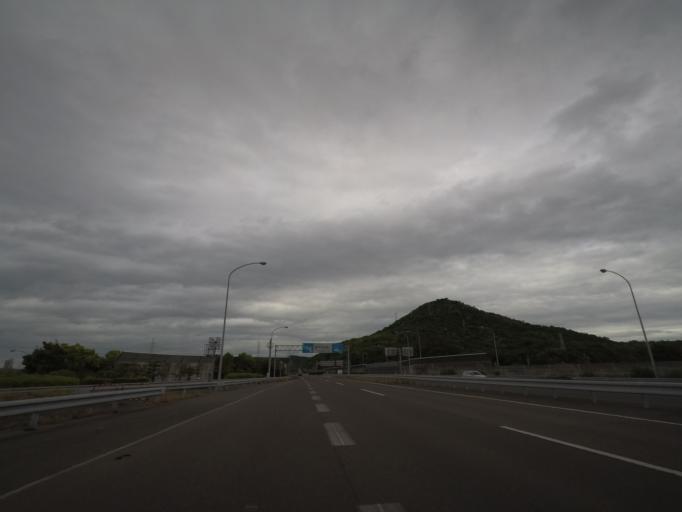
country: JP
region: Kagawa
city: Sakaidecho
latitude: 34.2979
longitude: 133.8439
